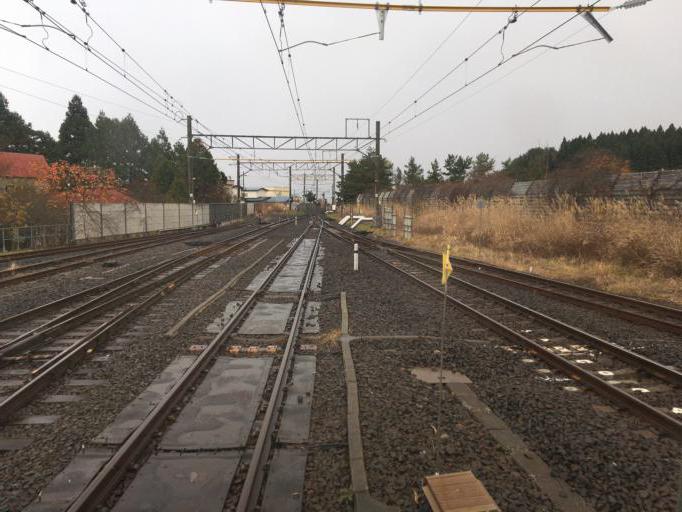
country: JP
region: Aomori
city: Aomori Shi
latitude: 41.0376
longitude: 140.6433
